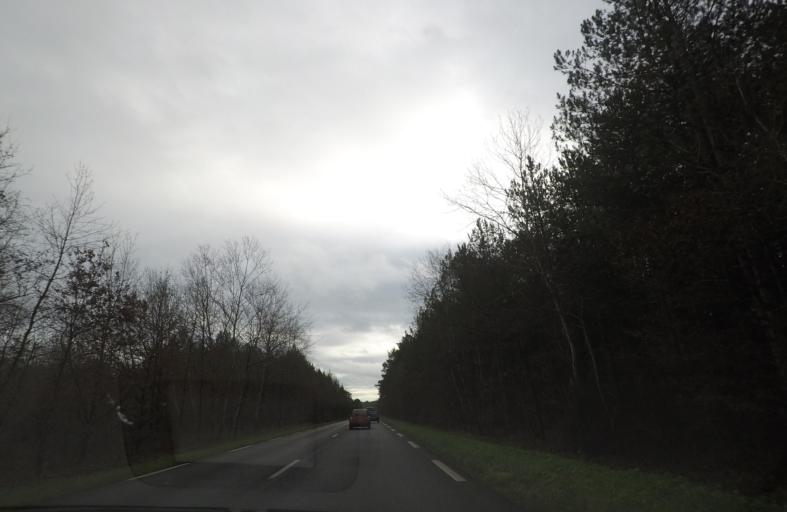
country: FR
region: Centre
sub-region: Departement du Loir-et-Cher
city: Mur-de-Sologne
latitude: 47.4023
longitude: 1.6314
